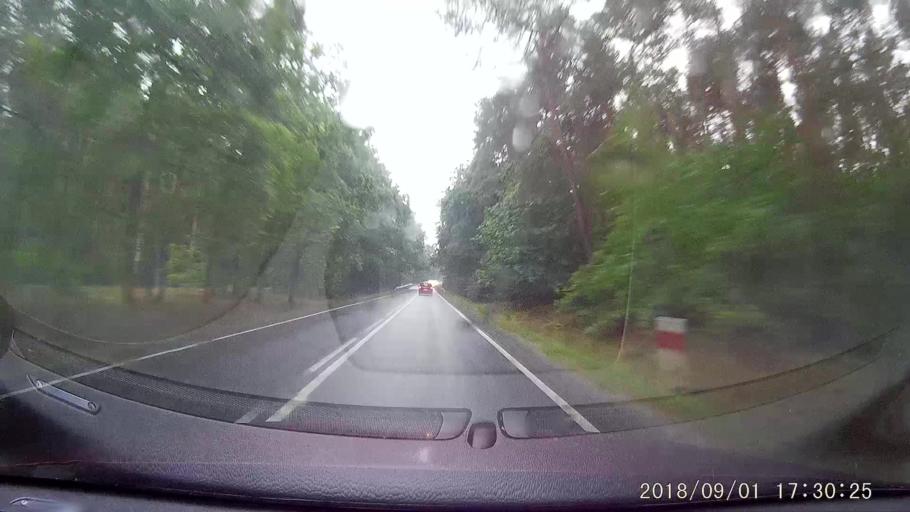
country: PL
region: Lubusz
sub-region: Powiat zaganski
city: Zagan
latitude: 51.6422
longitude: 15.3204
